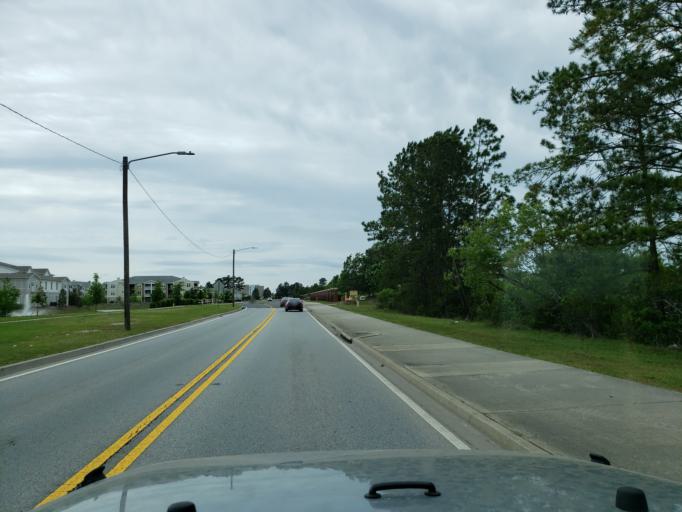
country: US
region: Georgia
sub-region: Chatham County
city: Pooler
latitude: 32.1511
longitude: -81.2447
